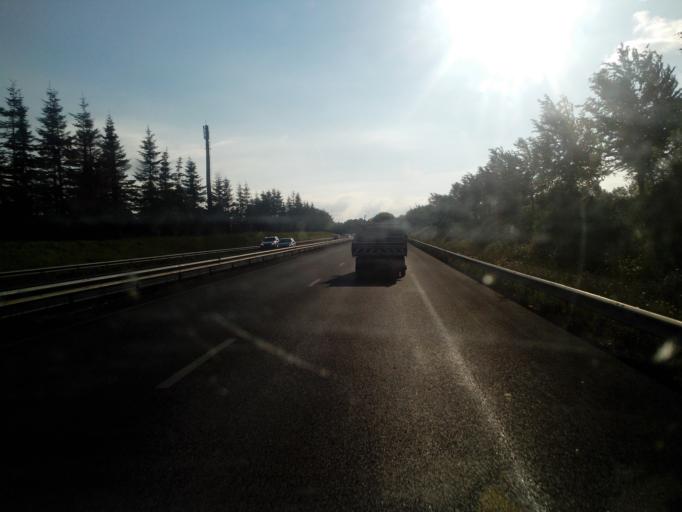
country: FR
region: Lower Normandy
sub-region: Departement du Calvados
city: Grainville-sur-Odon
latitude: 49.1437
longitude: -0.5277
